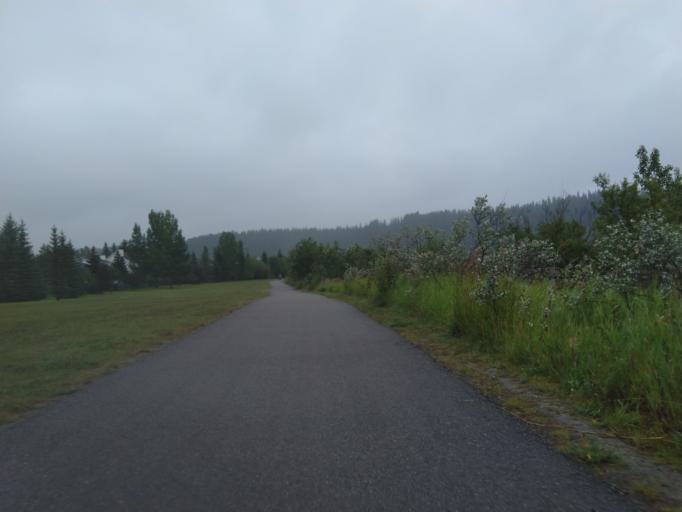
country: CA
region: Alberta
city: Cochrane
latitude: 51.1777
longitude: -114.4778
